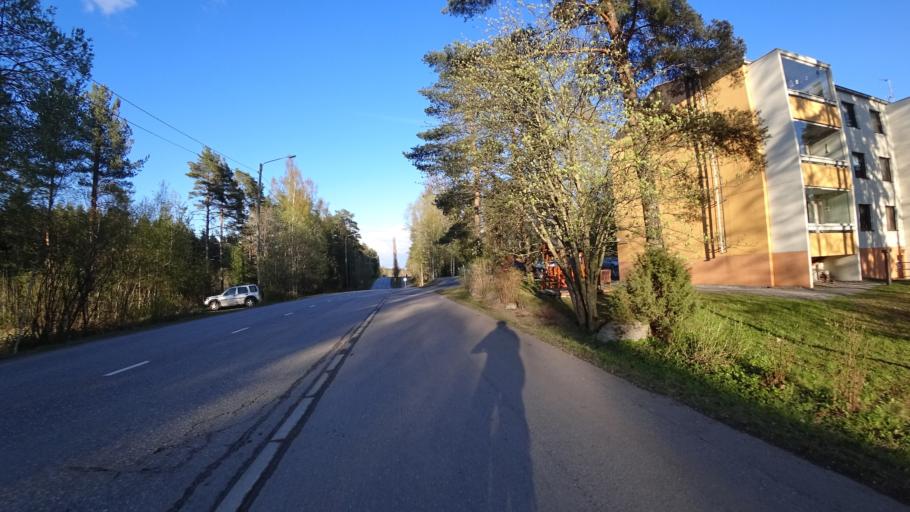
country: FI
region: Pirkanmaa
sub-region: Tampere
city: Nokia
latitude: 61.4912
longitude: 23.5355
